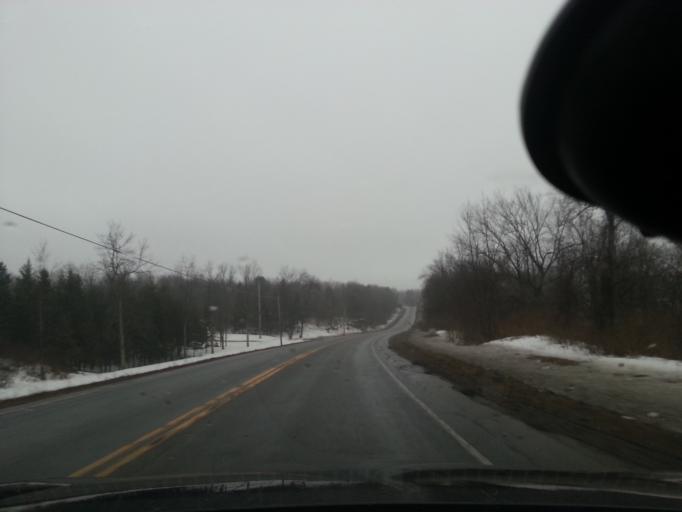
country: US
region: New York
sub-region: St. Lawrence County
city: Canton
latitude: 44.5060
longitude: -75.3402
